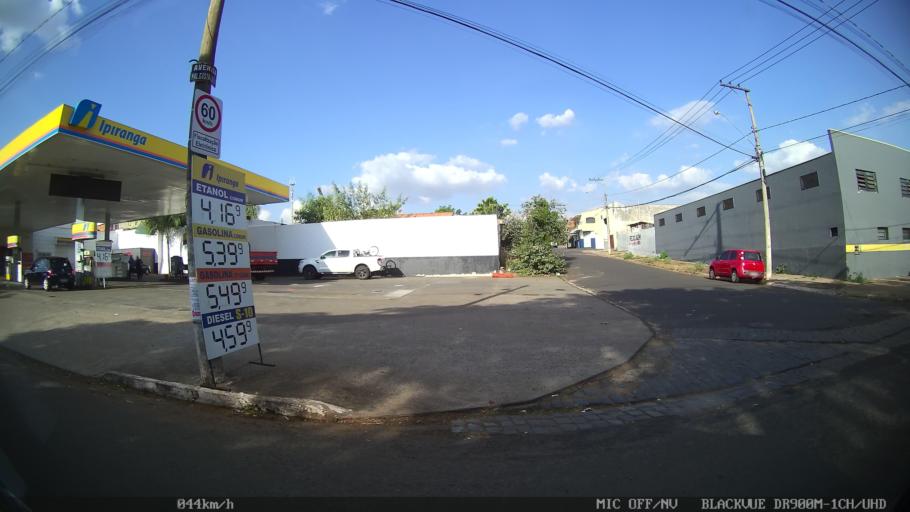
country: BR
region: Sao Paulo
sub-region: Ribeirao Preto
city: Ribeirao Preto
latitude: -21.1410
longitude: -47.7988
